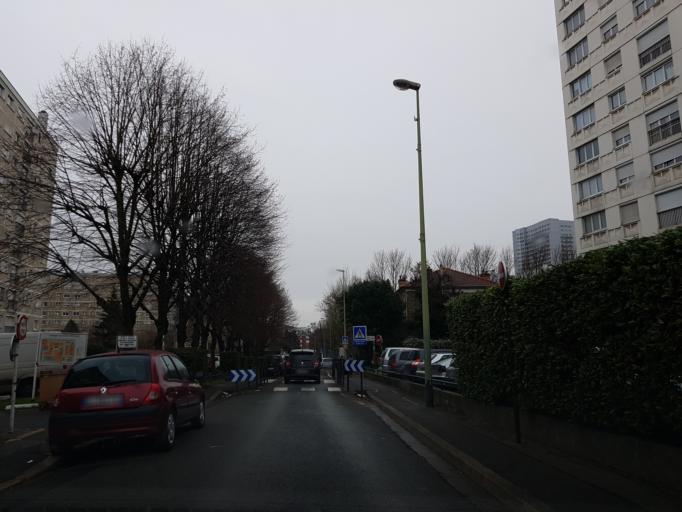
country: FR
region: Ile-de-France
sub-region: Departement du Val-de-Marne
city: Vitry-sur-Seine
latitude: 48.7945
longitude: 2.3905
